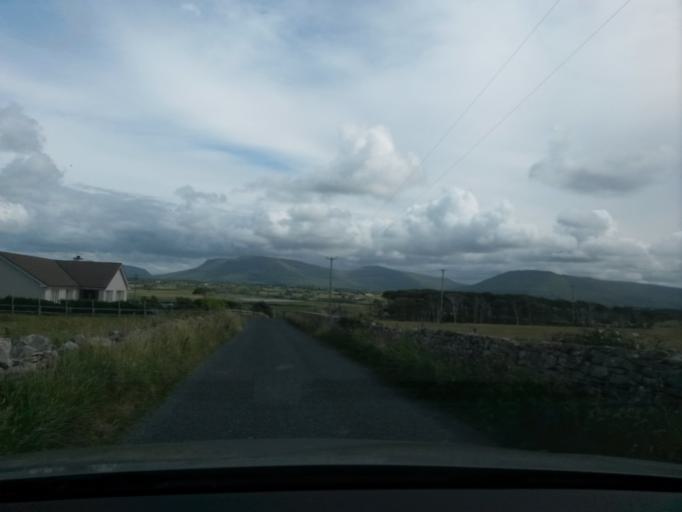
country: IE
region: Ulster
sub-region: County Donegal
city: Killybegs
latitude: 54.4595
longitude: -8.4587
